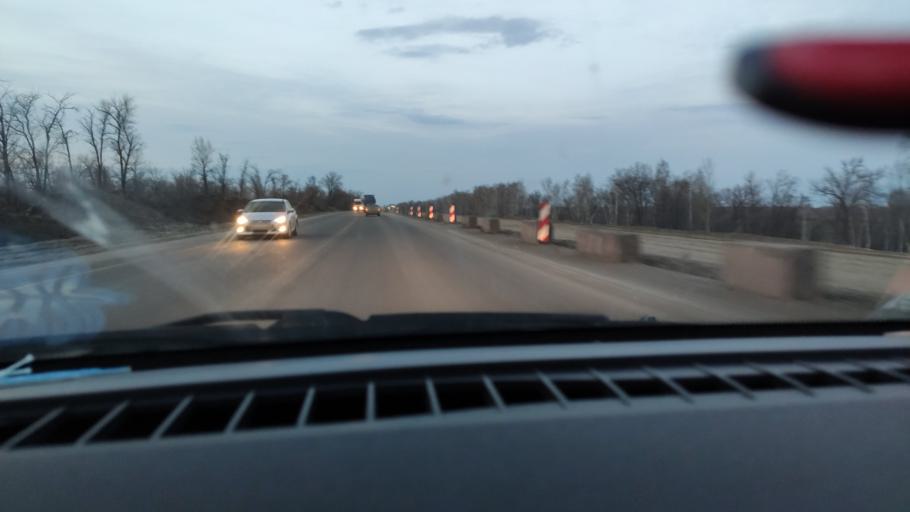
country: RU
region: Saratov
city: Sinodskoye
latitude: 52.0228
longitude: 46.7093
